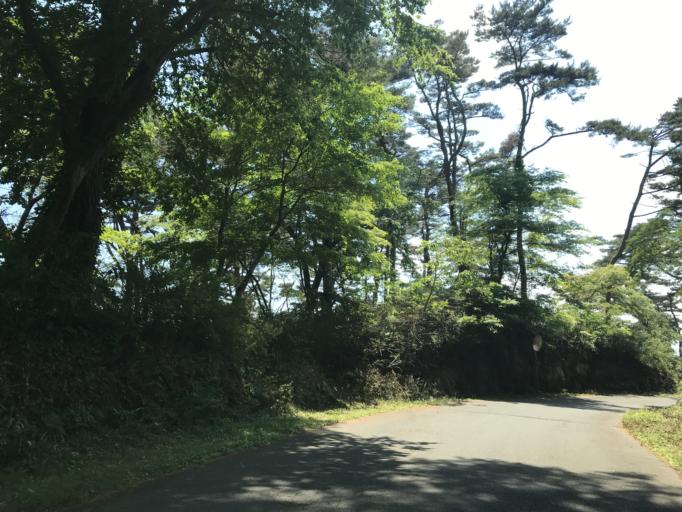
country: JP
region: Miyagi
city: Matsushima
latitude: 38.3526
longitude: 141.0639
